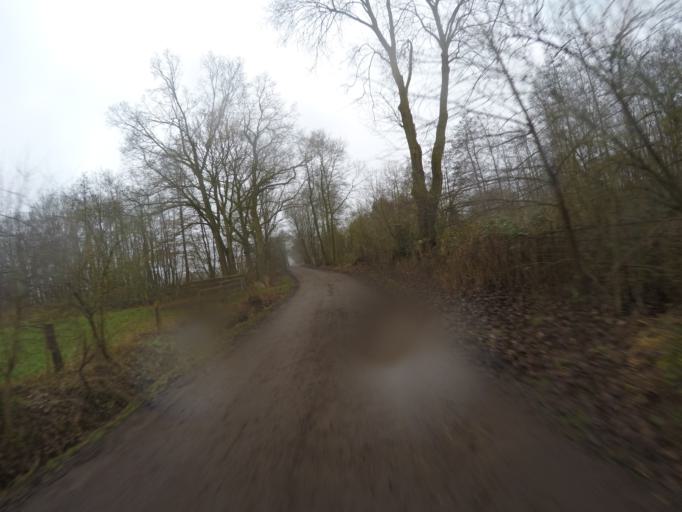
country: DE
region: Schleswig-Holstein
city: Ellerau
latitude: 53.7443
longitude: 9.9245
